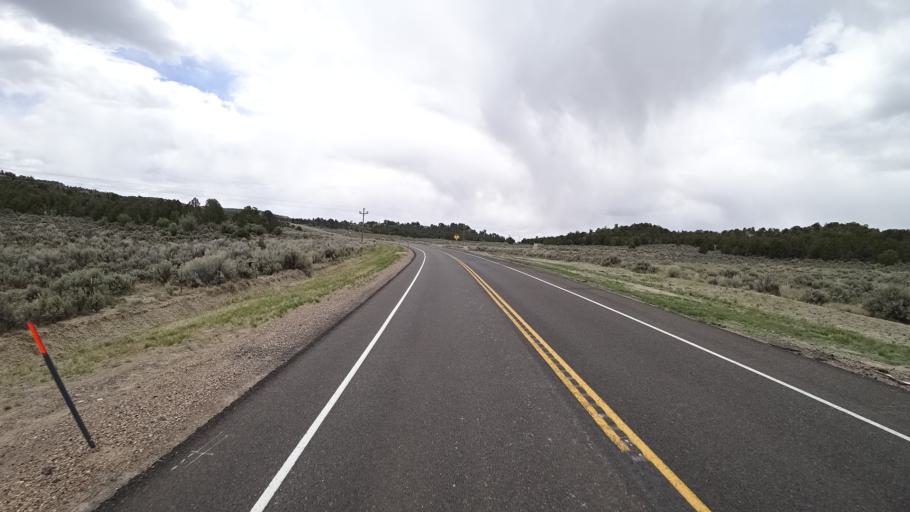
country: US
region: Utah
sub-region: Garfield County
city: Panguitch
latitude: 37.6478
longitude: -111.8449
